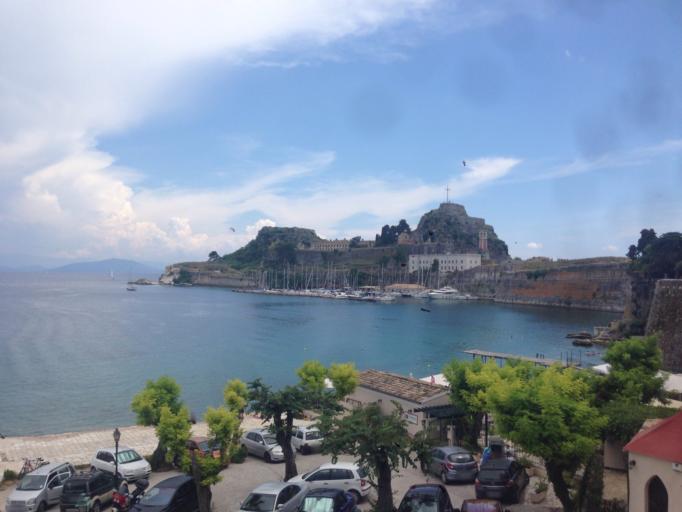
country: GR
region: Ionian Islands
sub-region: Nomos Kerkyras
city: Kerkyra
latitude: 39.6269
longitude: 19.9248
